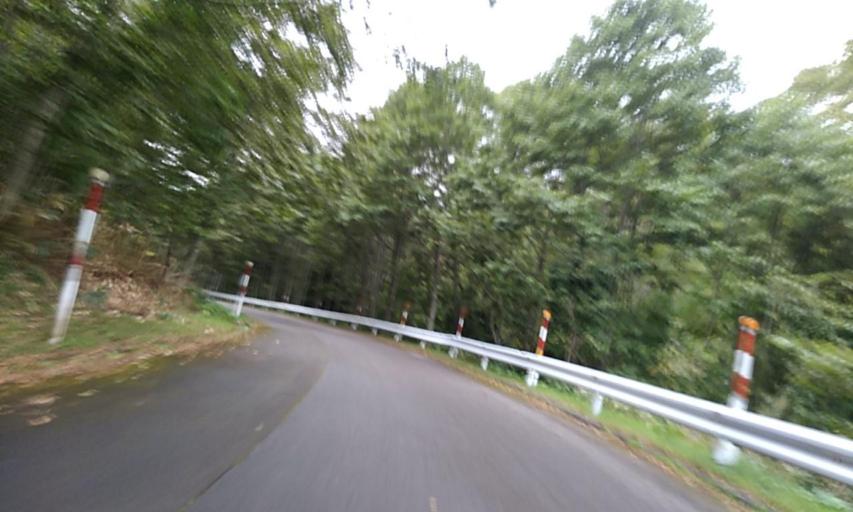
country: JP
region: Hokkaido
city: Bihoro
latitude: 43.5717
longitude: 144.1980
